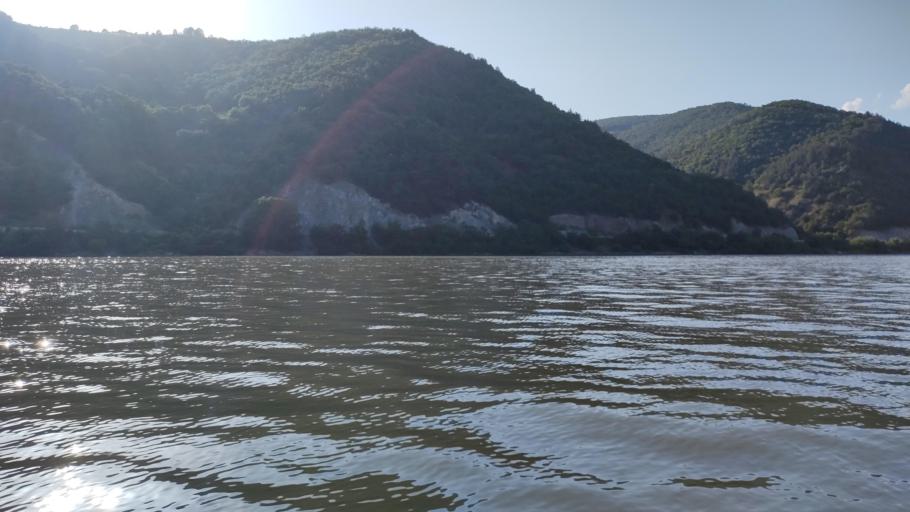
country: RO
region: Mehedinti
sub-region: Comuna Svinita
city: Svinita
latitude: 44.4969
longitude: 22.1896
